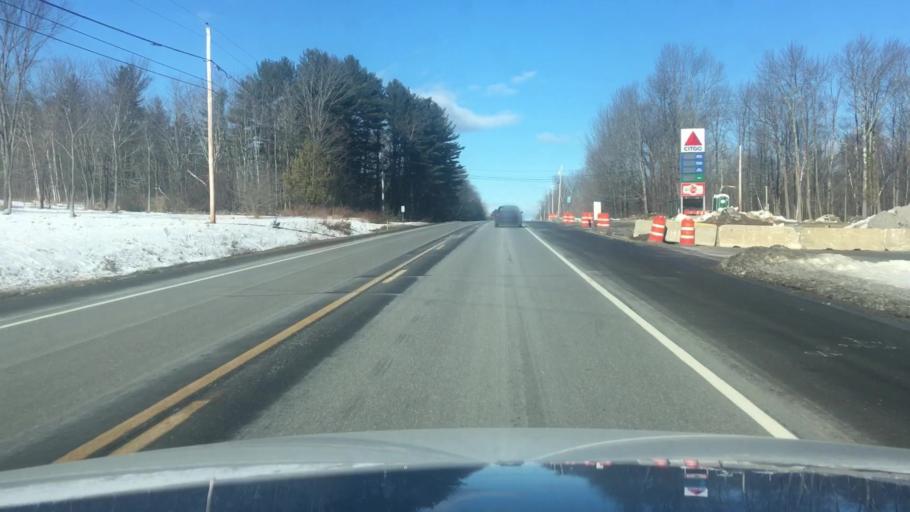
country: US
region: Maine
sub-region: Kennebec County
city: Waterville
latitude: 44.6197
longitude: -69.6711
